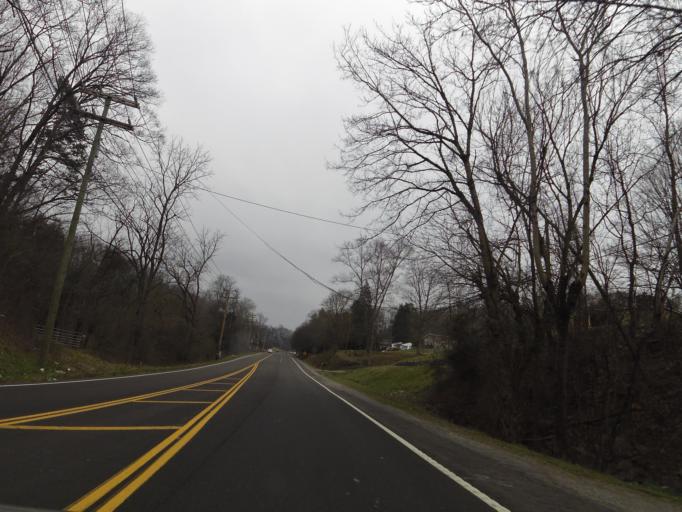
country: US
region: Tennessee
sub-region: Anderson County
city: Clinton
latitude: 36.1373
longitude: -84.1520
